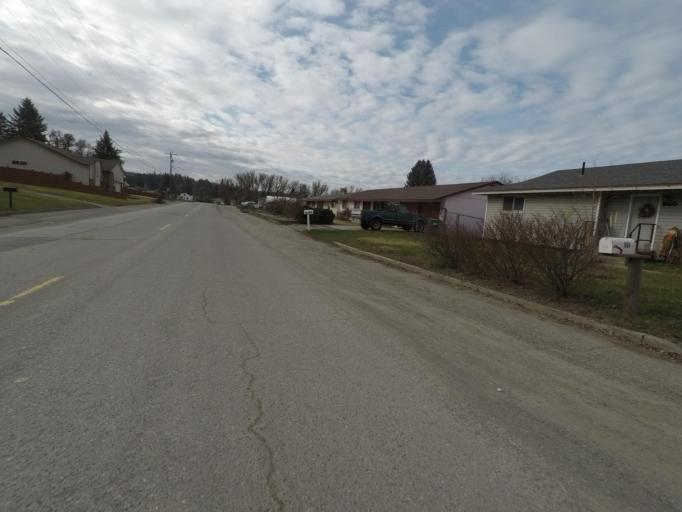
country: US
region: Washington
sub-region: Stevens County
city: Colville
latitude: 48.5356
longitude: -117.8854
